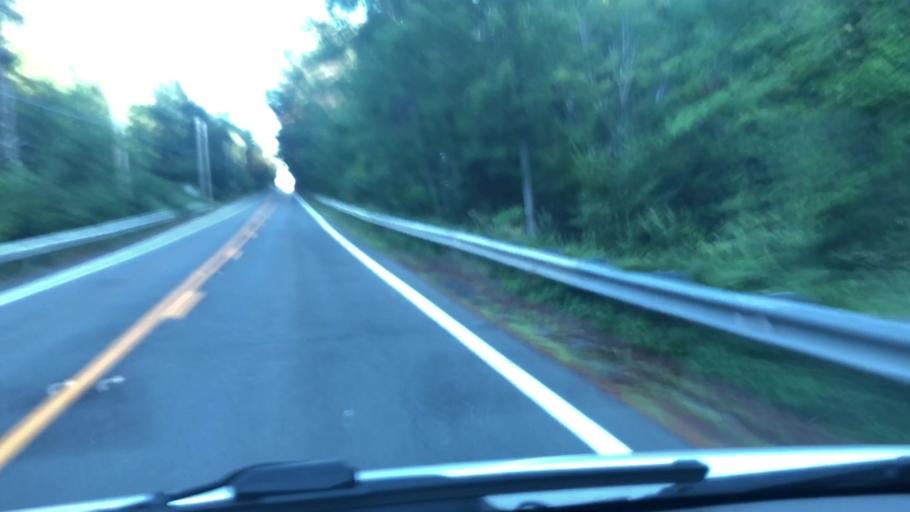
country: US
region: Massachusetts
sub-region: Hampshire County
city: Chesterfield
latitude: 42.3728
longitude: -72.9137
